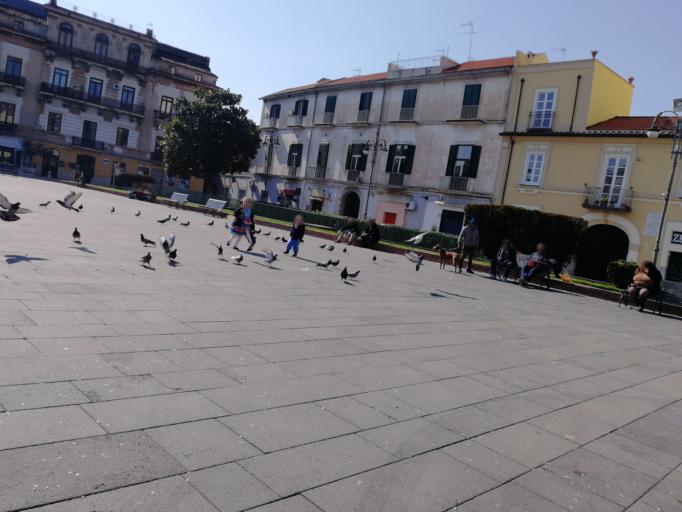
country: IT
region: Campania
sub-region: Provincia di Caserta
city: Santa Maria Capua Vetere
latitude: 41.0786
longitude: 14.2558
